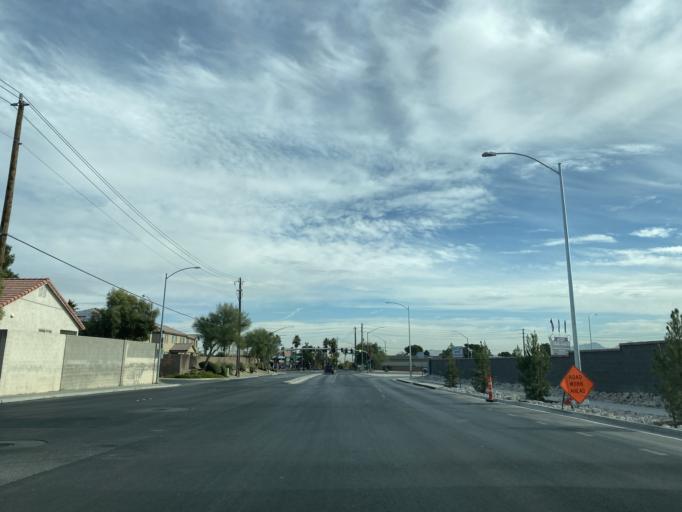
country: US
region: Nevada
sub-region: Clark County
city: North Las Vegas
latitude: 36.2469
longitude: -115.1566
